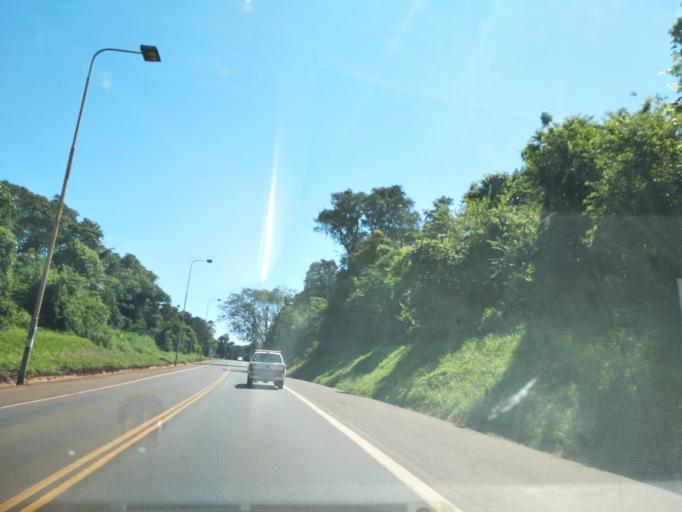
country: AR
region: Misiones
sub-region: Departamento de Iguazu
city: Puerto Iguazu
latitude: -25.6084
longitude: -54.5615
